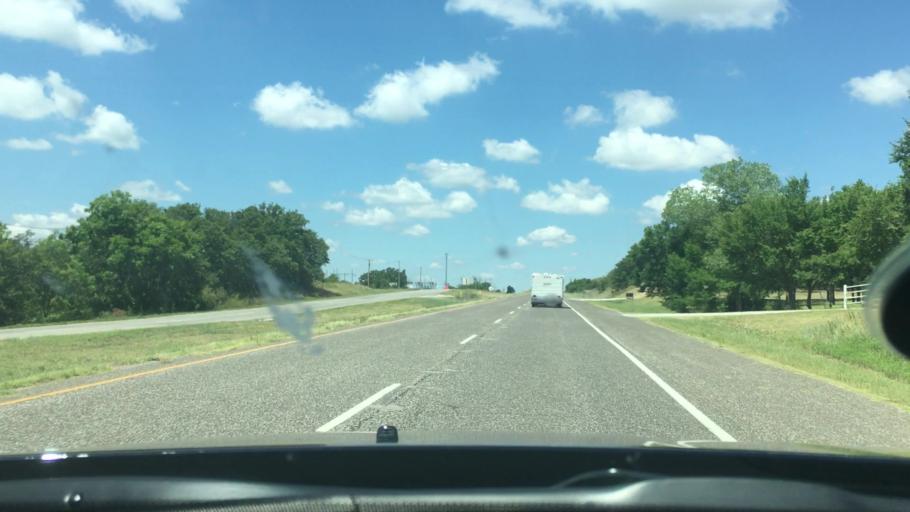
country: US
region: Oklahoma
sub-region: Carter County
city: Lone Grove
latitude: 34.1730
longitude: -97.3246
